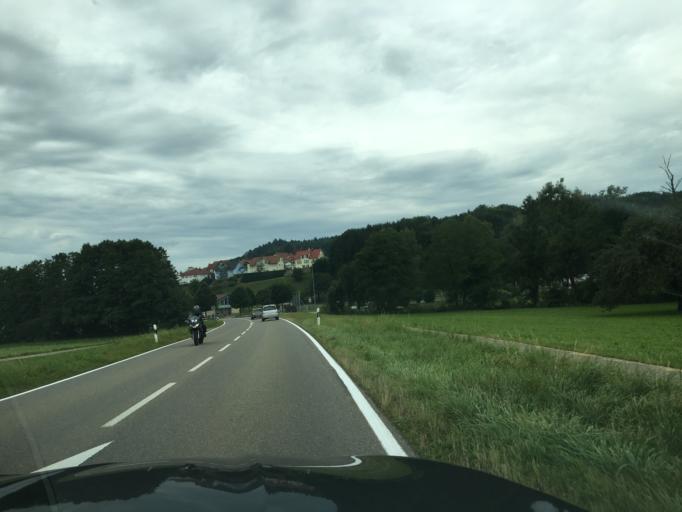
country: DE
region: Baden-Wuerttemberg
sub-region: Freiburg Region
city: Bodman-Ludwigshafen
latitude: 47.8592
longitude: 9.0672
